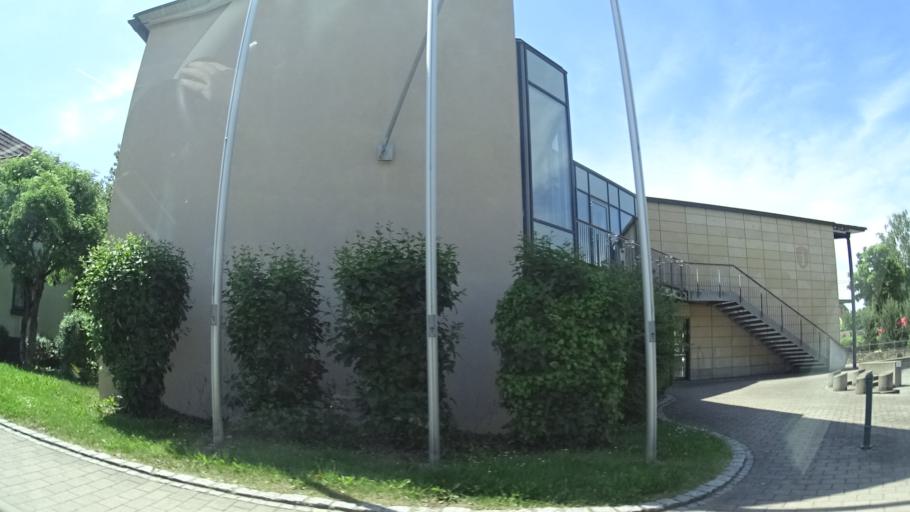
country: DE
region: Bavaria
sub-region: Regierungsbezirk Unterfranken
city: Poppenhausen
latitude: 50.0995
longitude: 10.1440
